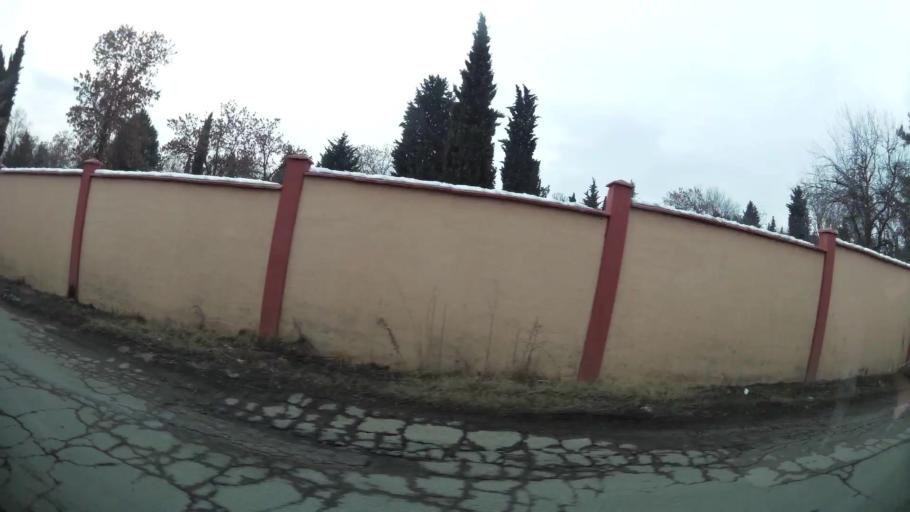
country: MK
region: Butel
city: Butel
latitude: 42.0359
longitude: 21.4364
